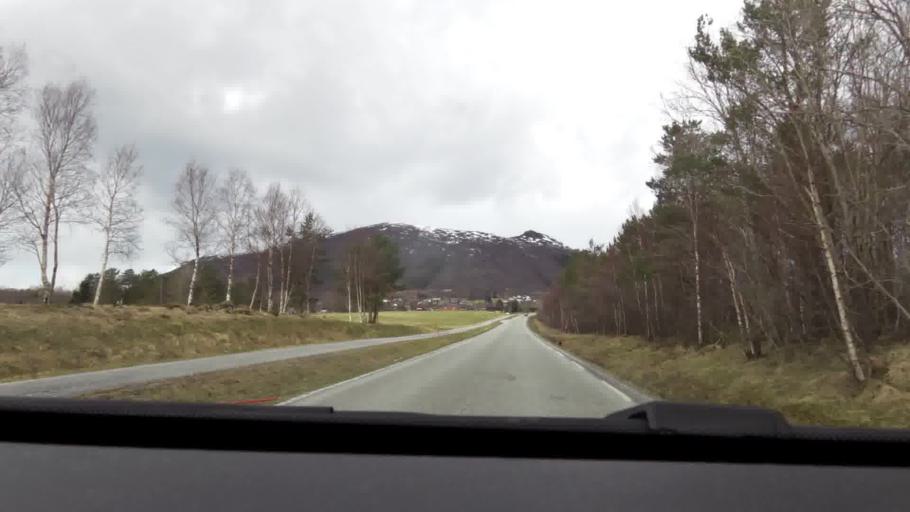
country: NO
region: More og Romsdal
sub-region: Eide
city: Eide
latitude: 62.9078
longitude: 7.4449
